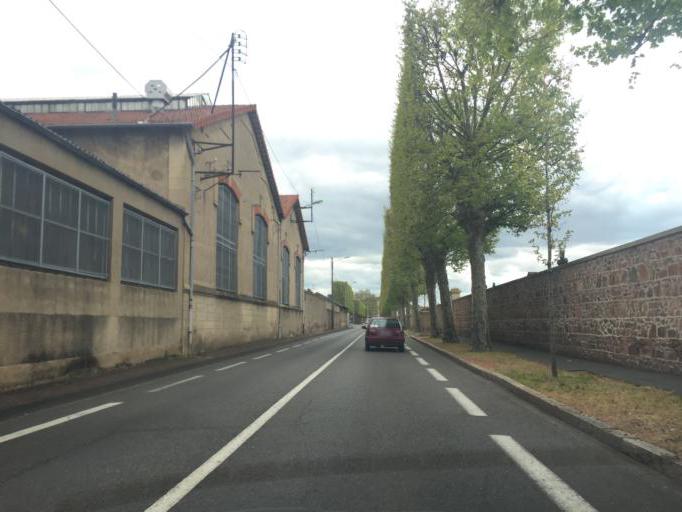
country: FR
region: Rhone-Alpes
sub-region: Departement de la Loire
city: Roanne
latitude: 46.0514
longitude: 4.0718
